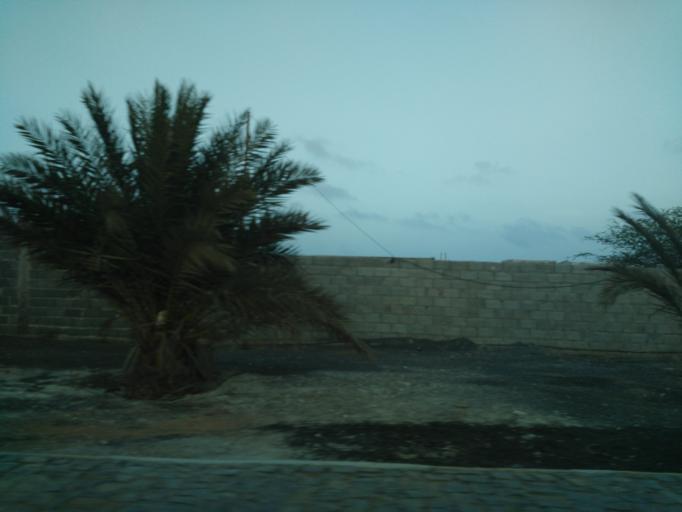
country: CV
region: Sal
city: Santa Maria
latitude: 16.6143
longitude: -22.9240
